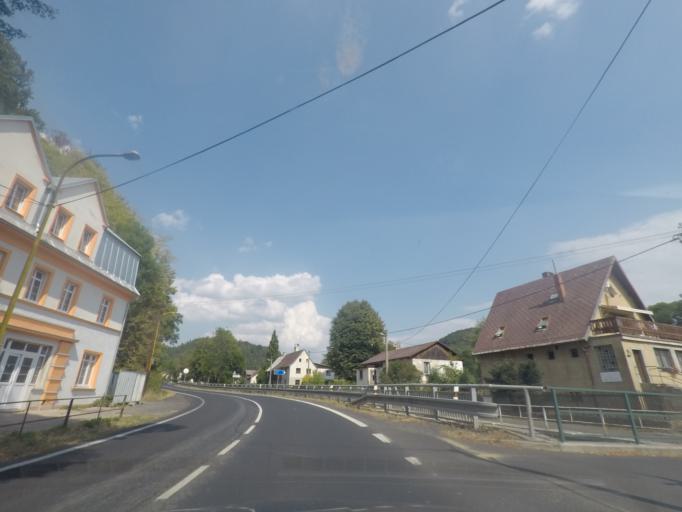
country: CZ
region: Ustecky
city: Ceska Kamenice
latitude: 50.8015
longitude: 14.4387
